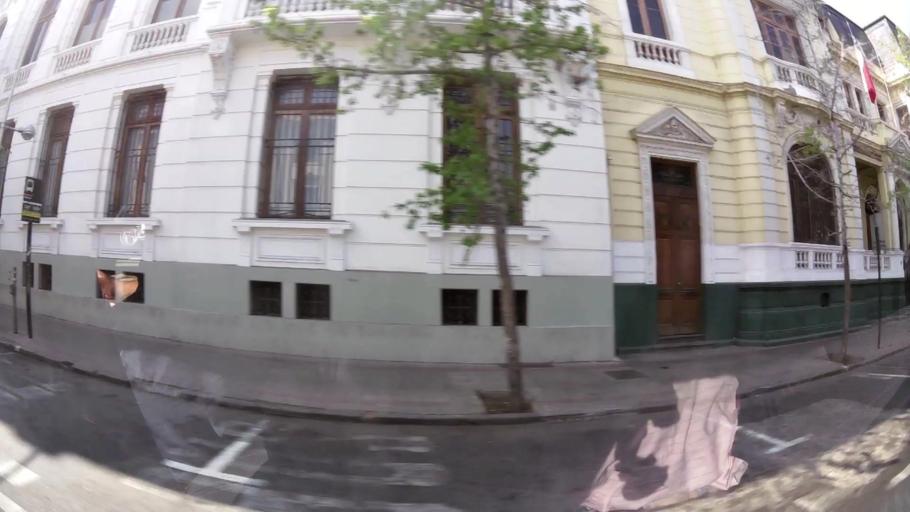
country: CL
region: Santiago Metropolitan
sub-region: Provincia de Santiago
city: Santiago
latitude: -33.4475
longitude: -70.6581
